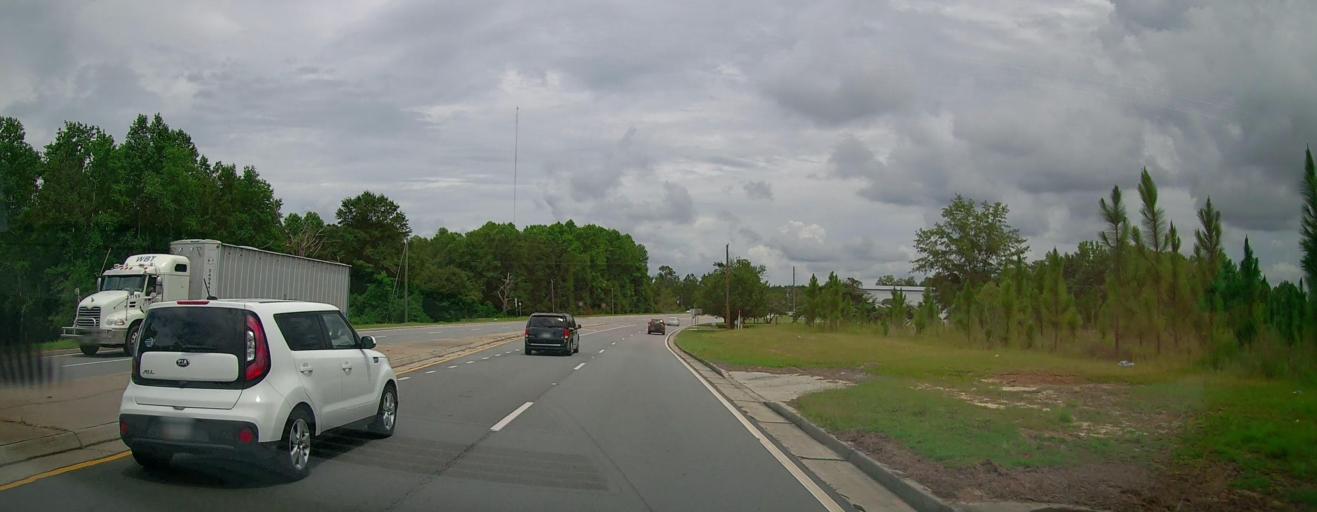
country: US
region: Georgia
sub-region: Telfair County
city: McRae
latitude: 32.0580
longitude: -82.8693
